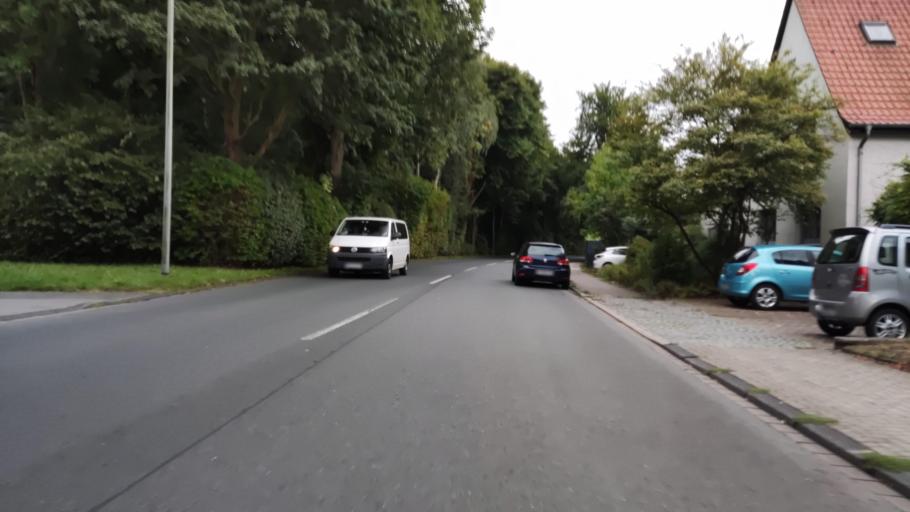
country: DE
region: North Rhine-Westphalia
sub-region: Regierungsbezirk Arnsberg
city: Herne
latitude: 51.5350
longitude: 7.2374
